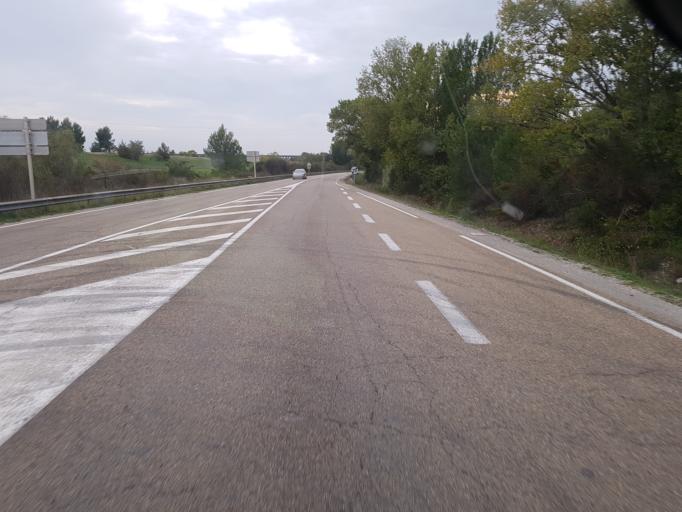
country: FR
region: Provence-Alpes-Cote d'Azur
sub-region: Departement du Vaucluse
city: Avignon
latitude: 43.9464
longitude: 4.7853
